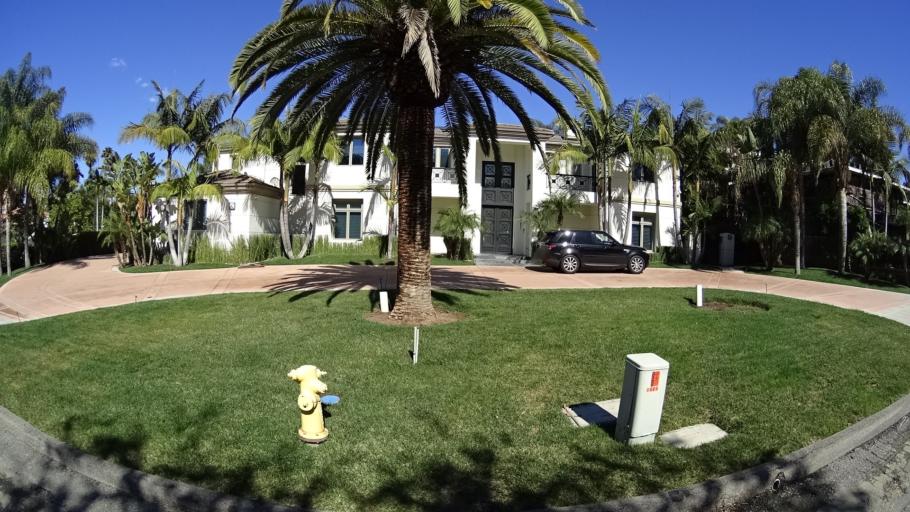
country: US
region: California
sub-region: Orange County
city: Villa Park
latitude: 33.8476
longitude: -117.8115
